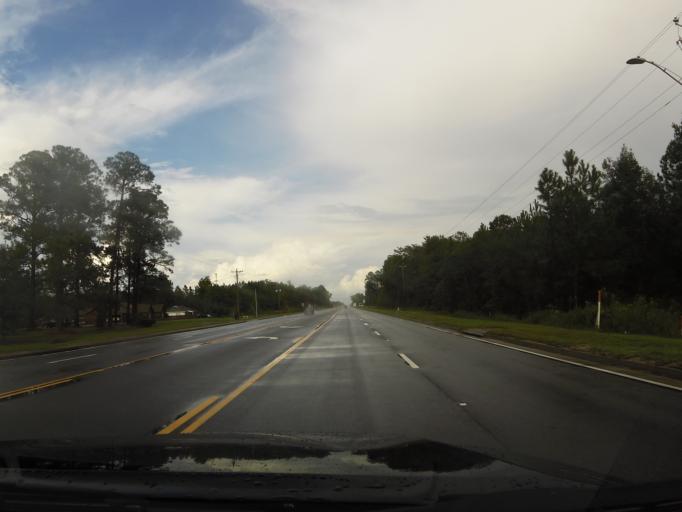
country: US
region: Georgia
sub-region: Long County
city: Ludowici
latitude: 31.7166
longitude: -81.7394
